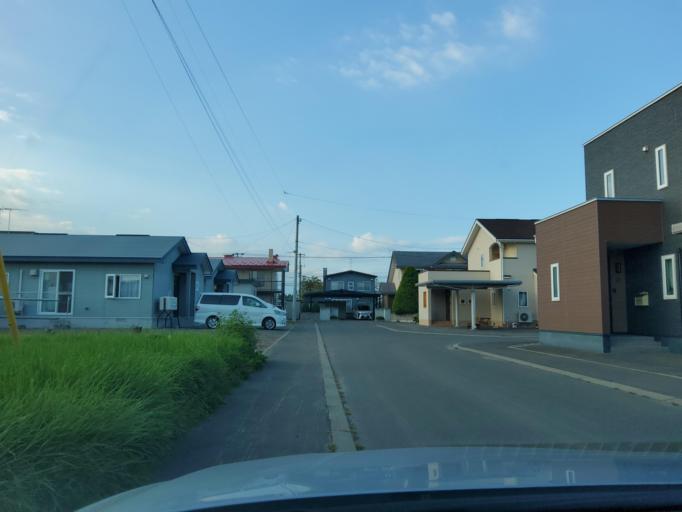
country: JP
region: Hokkaido
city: Obihiro
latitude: 42.9347
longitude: 143.1809
